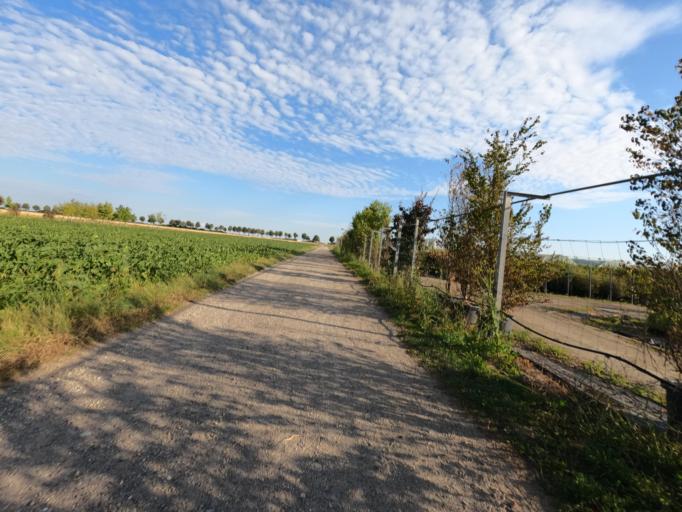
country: DE
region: North Rhine-Westphalia
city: Huckelhoven
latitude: 51.0880
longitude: 6.2548
